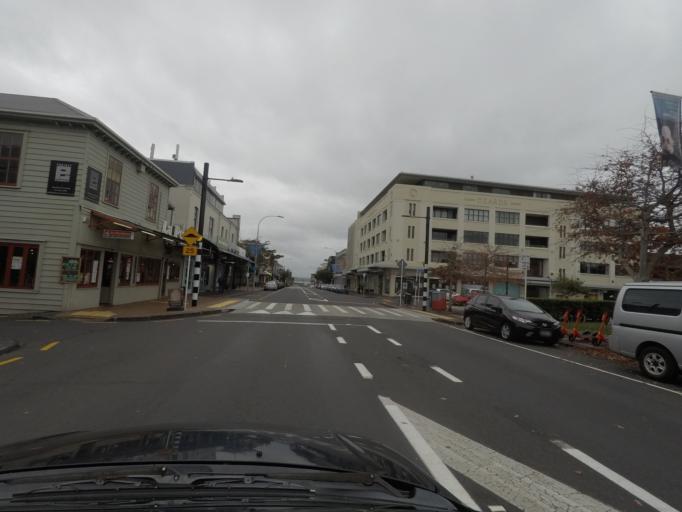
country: NZ
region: Auckland
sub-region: Auckland
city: Auckland
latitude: -36.8545
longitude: 174.7799
